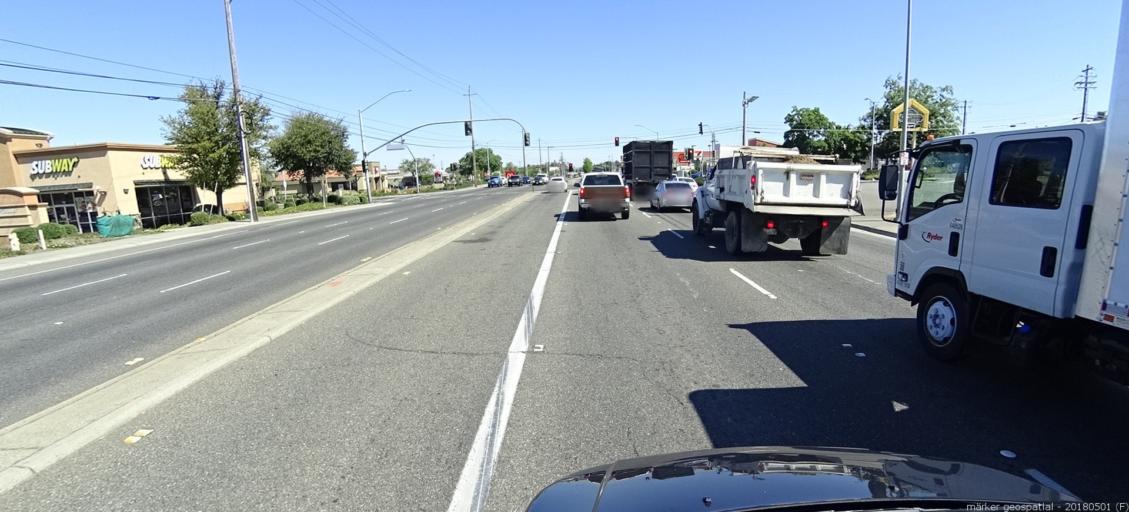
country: US
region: California
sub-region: Sacramento County
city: North Highlands
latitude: 38.6530
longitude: -121.3829
